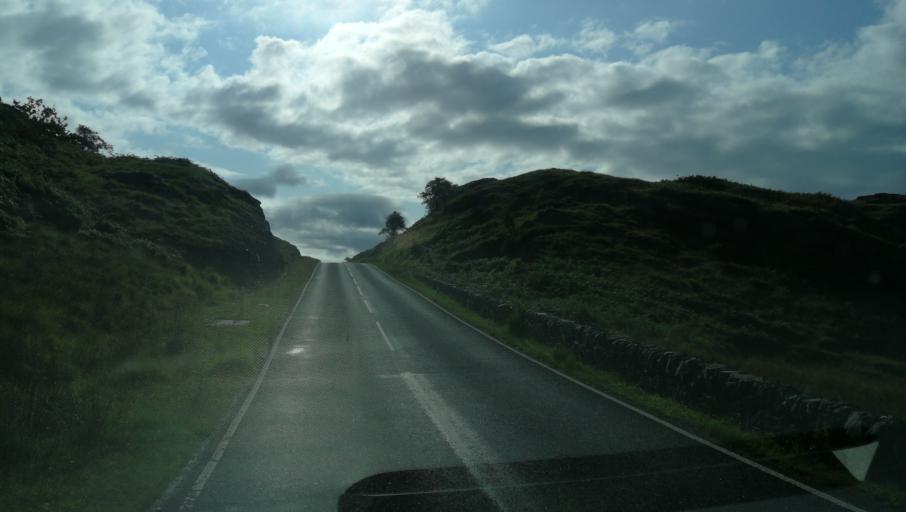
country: GB
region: Scotland
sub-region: Argyll and Bute
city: Isle Of Mull
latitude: 56.6794
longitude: -5.8508
